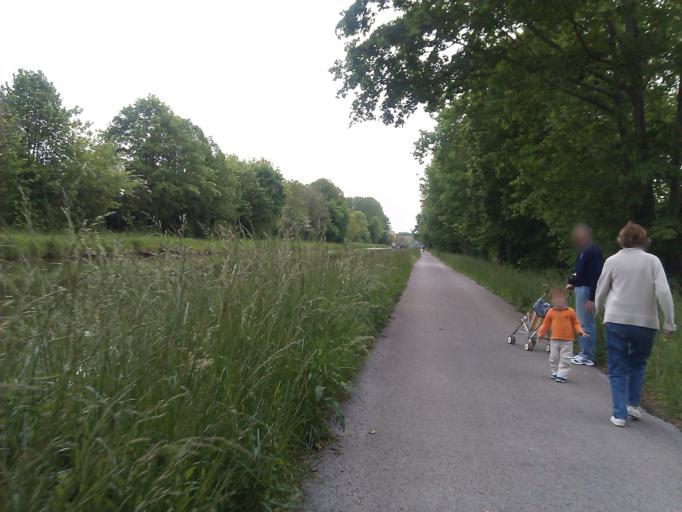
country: FR
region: Franche-Comte
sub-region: Departement du Jura
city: Dampierre
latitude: 47.1536
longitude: 5.7463
